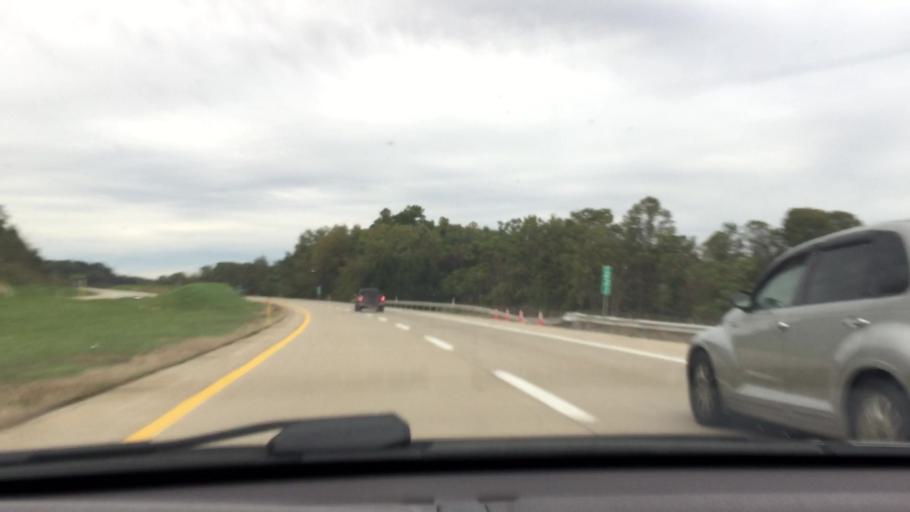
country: US
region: Pennsylvania
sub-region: Lawrence County
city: New Beaver
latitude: 40.8754
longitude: -80.3671
